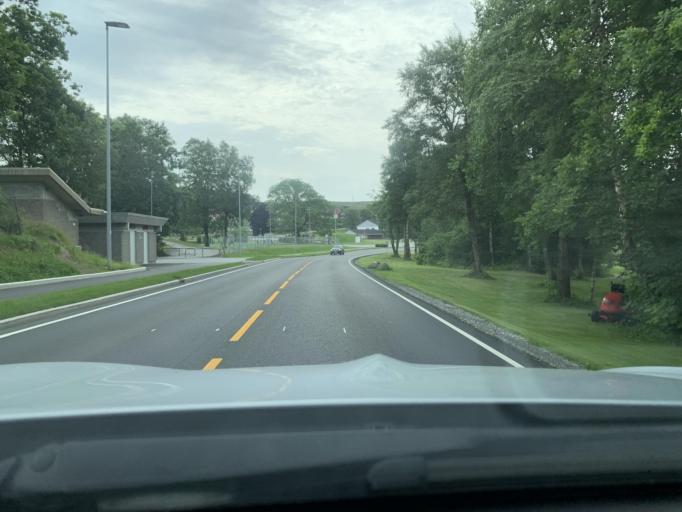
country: NO
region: Rogaland
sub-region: Sandnes
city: Sandnes
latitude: 58.7743
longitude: 5.7245
